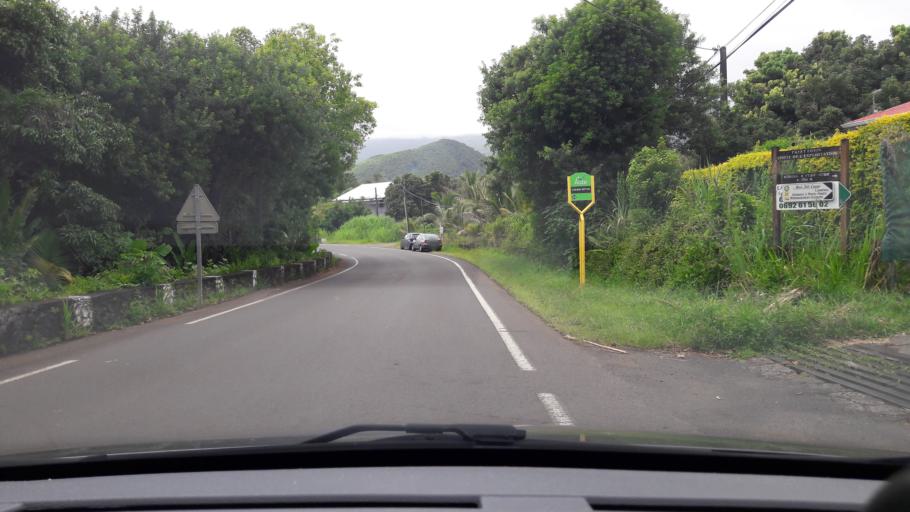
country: RE
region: Reunion
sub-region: Reunion
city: Saint-Benoit
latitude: -21.0884
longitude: 55.7004
